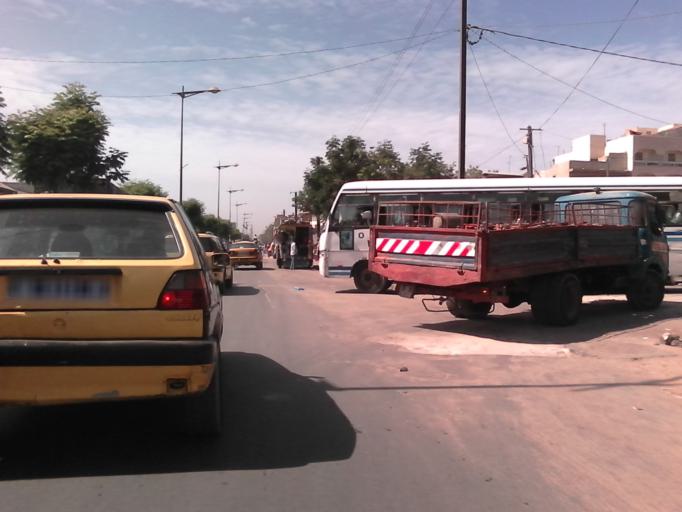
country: SN
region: Dakar
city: Grand Dakar
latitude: 14.7085
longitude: -17.4532
